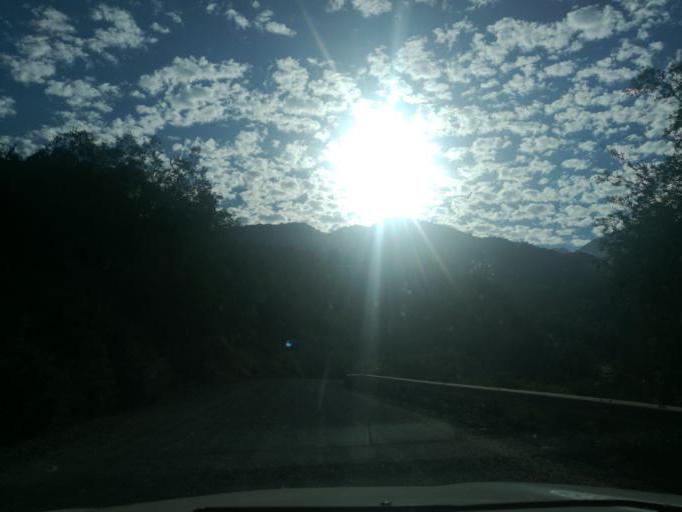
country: CL
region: O'Higgins
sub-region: Provincia de Cachapoal
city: Machali
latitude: -34.2539
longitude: -70.4656
